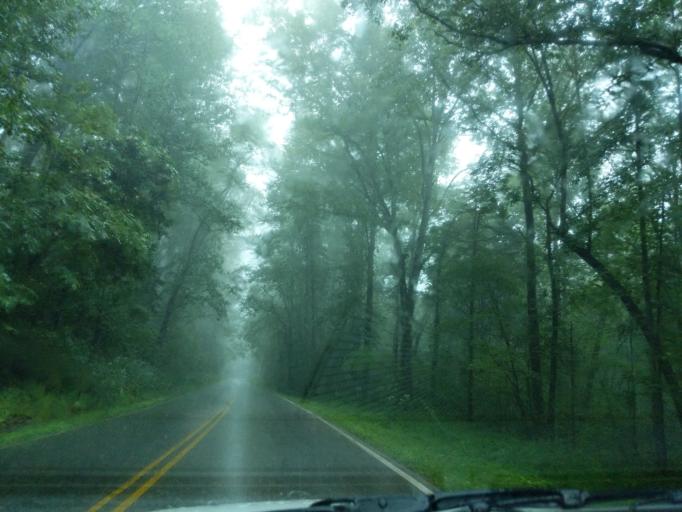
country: US
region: Kentucky
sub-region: Barren County
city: Cave City
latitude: 37.1578
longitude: -86.0983
